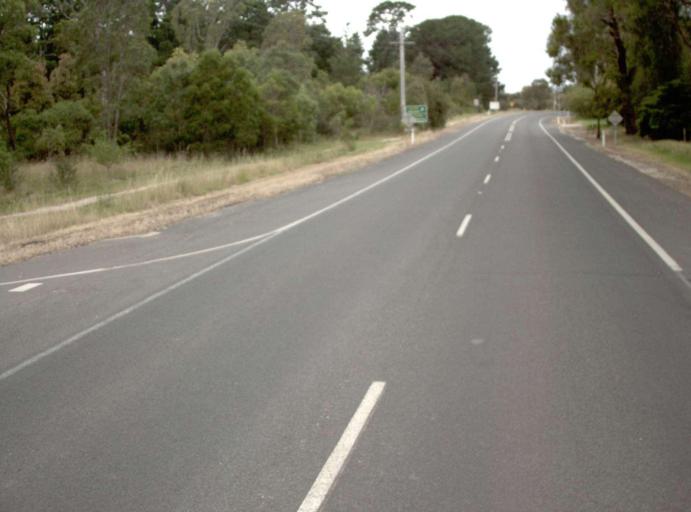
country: AU
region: Victoria
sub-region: Wellington
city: Sale
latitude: -38.1706
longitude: 147.0878
